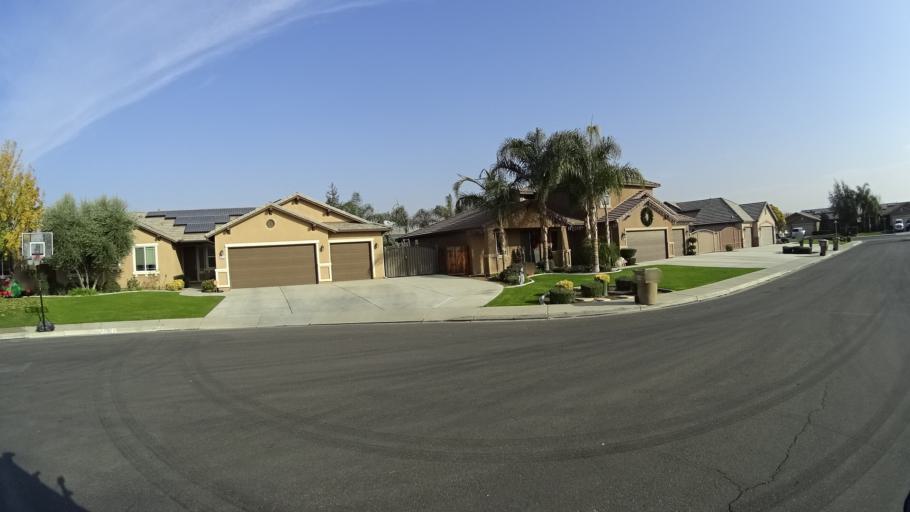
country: US
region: California
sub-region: Kern County
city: Greenacres
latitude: 35.4302
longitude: -119.1205
